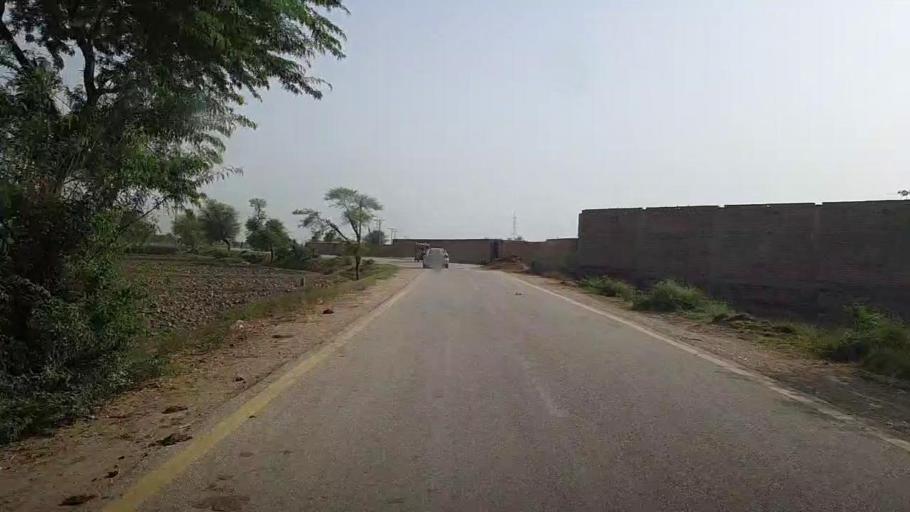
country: PK
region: Sindh
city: Khairpur Nathan Shah
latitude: 27.1032
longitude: 67.7570
